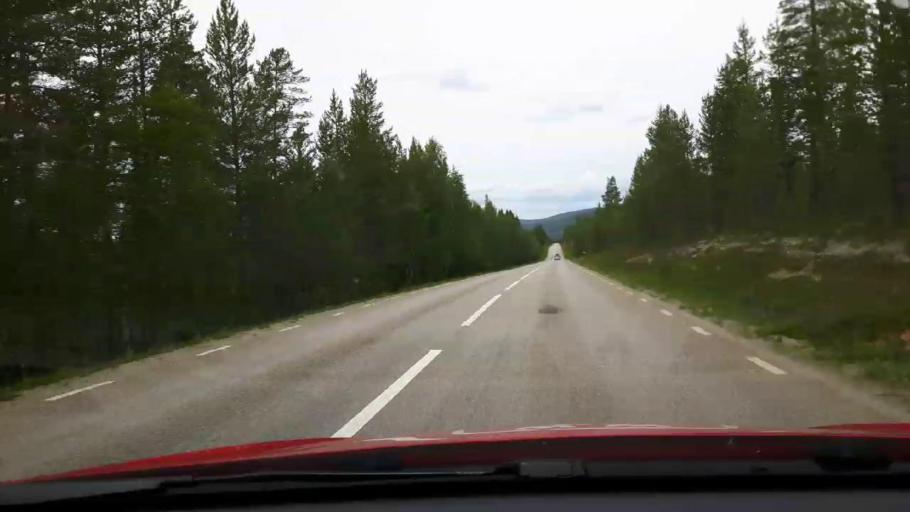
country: SE
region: Jaemtland
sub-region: Harjedalens Kommun
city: Sveg
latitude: 62.2470
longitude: 13.8433
